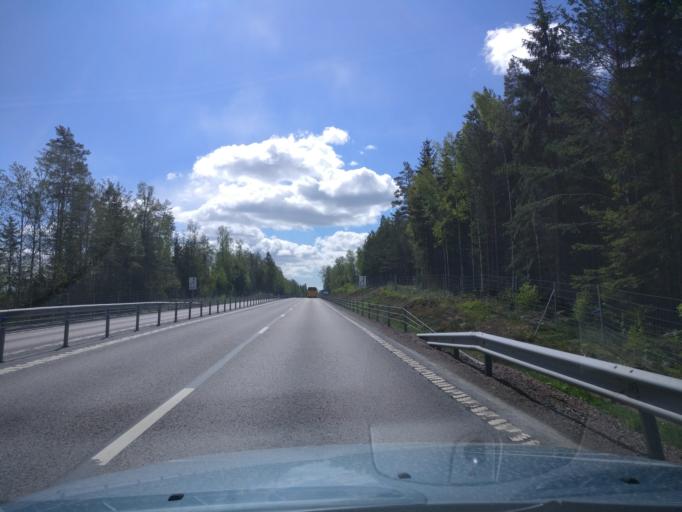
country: SE
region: Vaermland
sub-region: Karlstads Kommun
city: Karlstad
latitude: 59.4435
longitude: 13.5441
